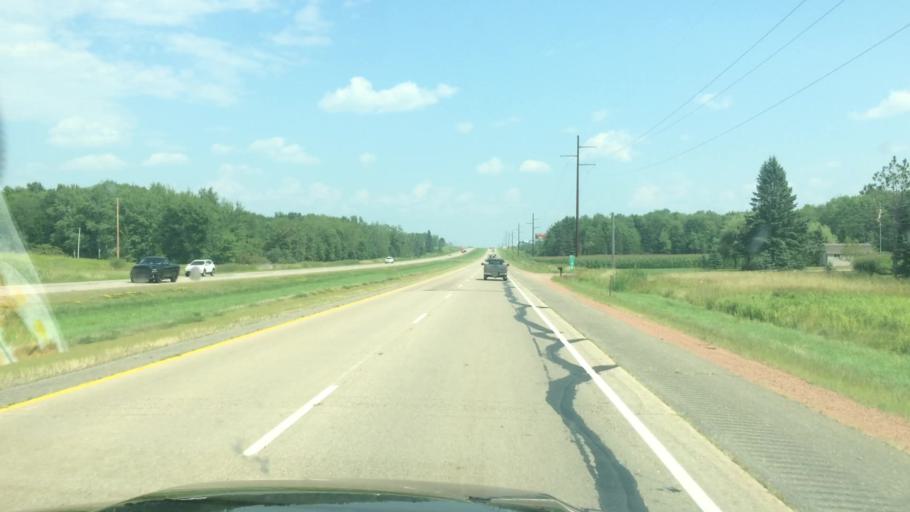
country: US
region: Wisconsin
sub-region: Marathon County
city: Edgar
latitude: 44.9441
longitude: -90.0207
